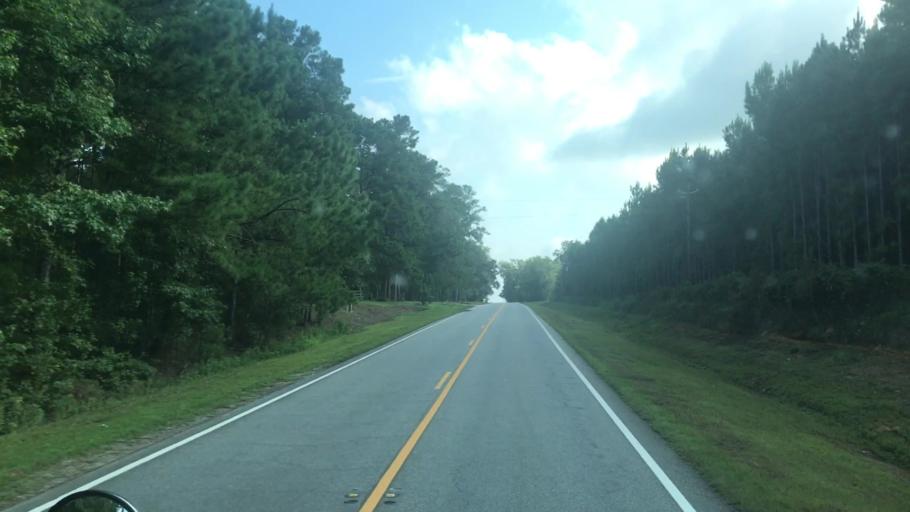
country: US
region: Florida
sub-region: Gadsden County
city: Havana
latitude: 30.7672
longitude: -84.4881
